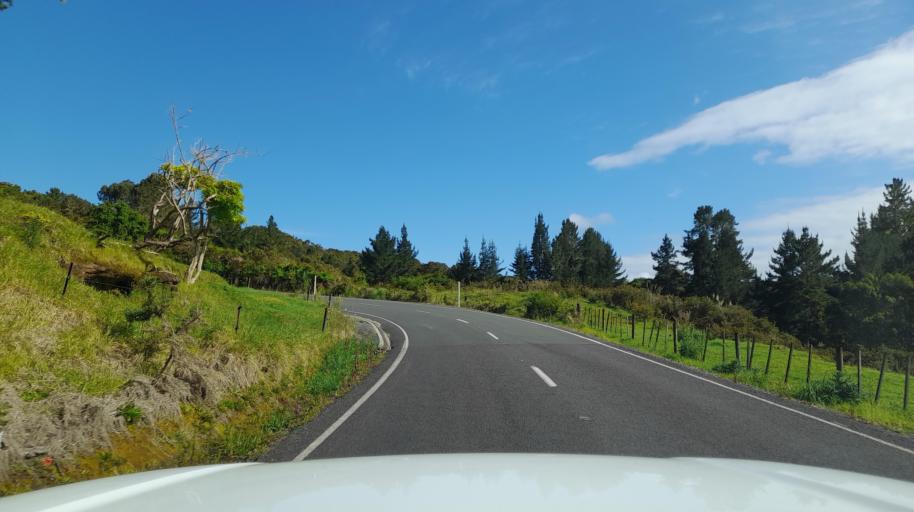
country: NZ
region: Northland
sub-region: Far North District
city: Moerewa
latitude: -35.4073
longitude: 173.9651
